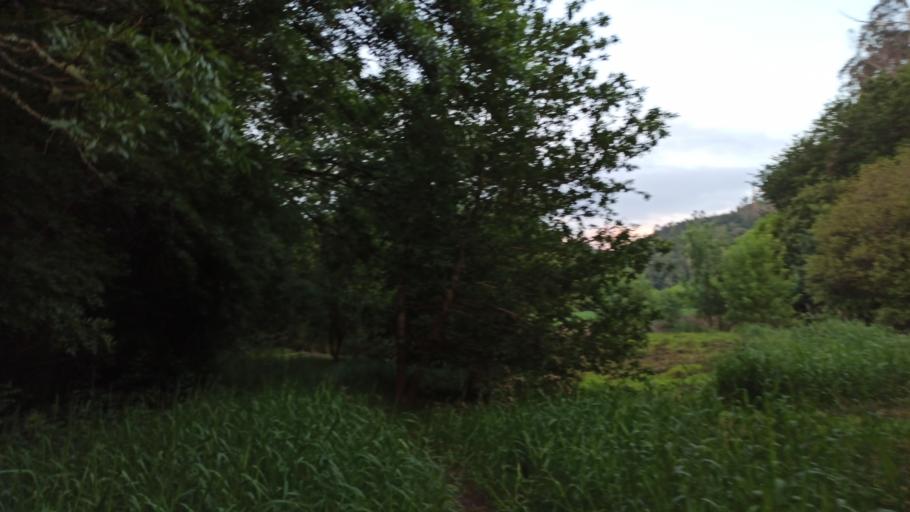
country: ES
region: Galicia
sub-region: Provincia da Coruna
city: Negreira
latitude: 42.9011
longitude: -8.7379
